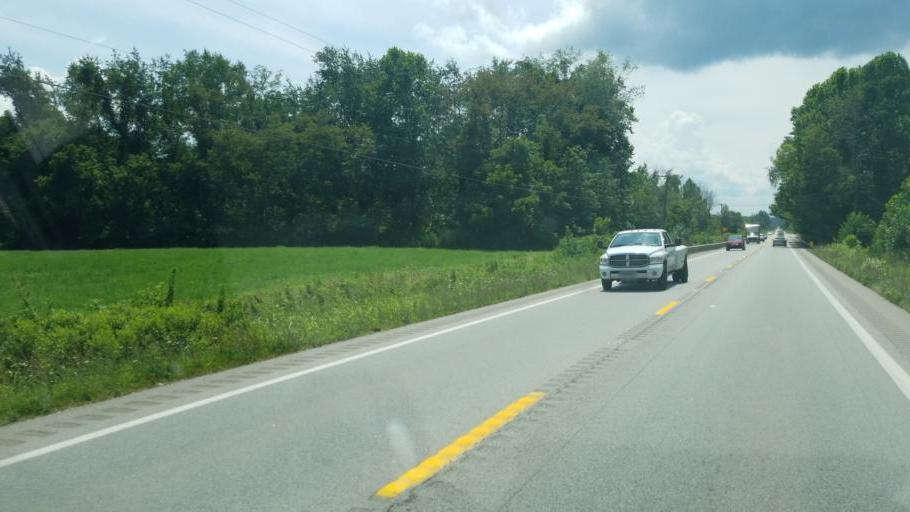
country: US
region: West Virginia
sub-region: Putnam County
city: Buffalo
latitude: 38.6258
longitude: -81.9834
